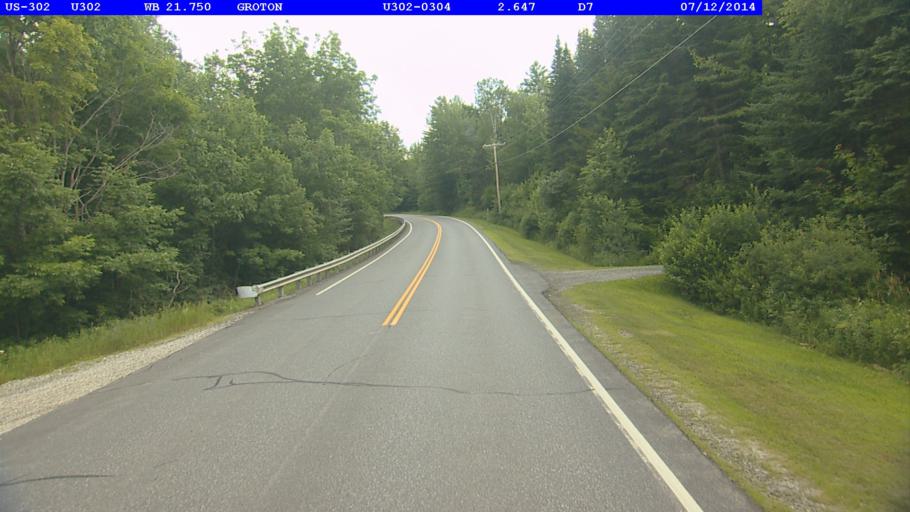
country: US
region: New Hampshire
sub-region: Grafton County
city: Woodsville
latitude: 44.2085
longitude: -72.2628
